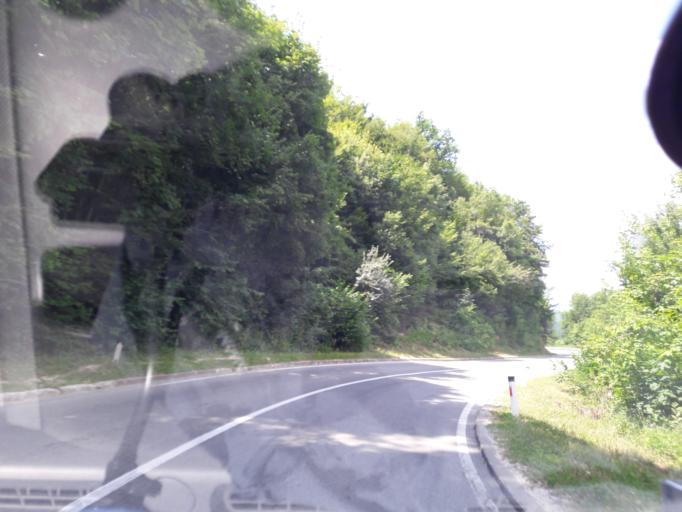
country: BA
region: Republika Srpska
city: Sipovo
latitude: 44.2046
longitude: 17.1410
